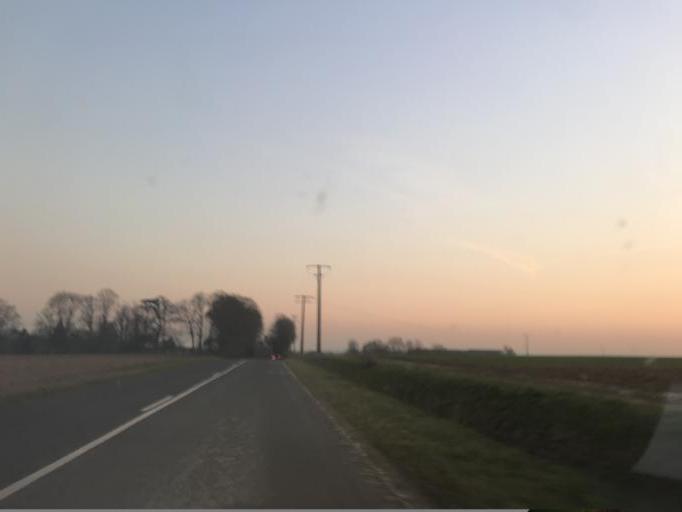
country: FR
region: Ile-de-France
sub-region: Departement de Seine-et-Marne
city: Juilly
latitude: 49.0060
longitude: 2.7003
